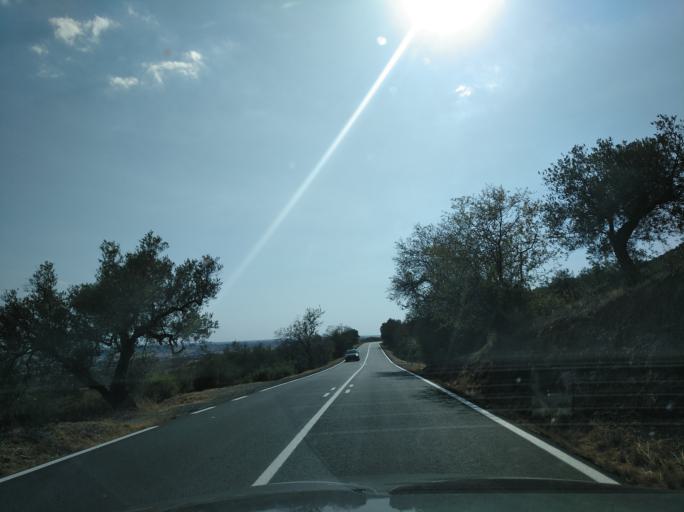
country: ES
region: Andalusia
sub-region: Provincia de Huelva
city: Rosal de la Frontera
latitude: 37.9567
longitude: -7.2668
